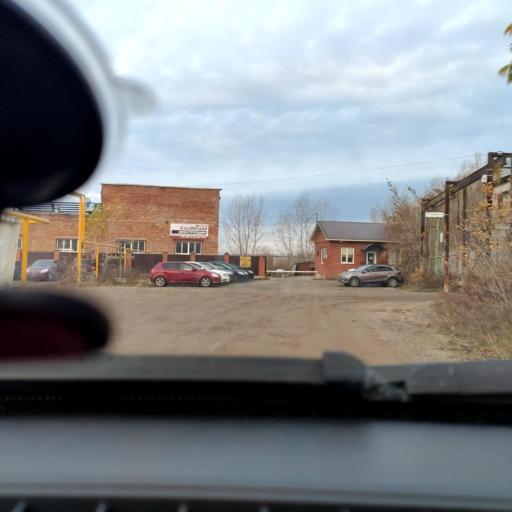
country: RU
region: Bashkortostan
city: Ufa
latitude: 54.7480
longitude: 55.9225
